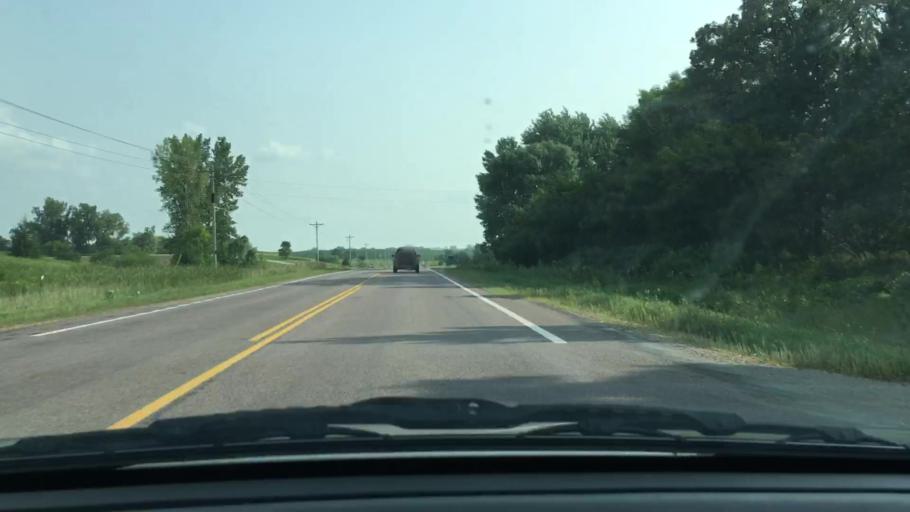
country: US
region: Minnesota
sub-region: Scott County
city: Elko New Market
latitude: 44.5511
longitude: -93.3394
